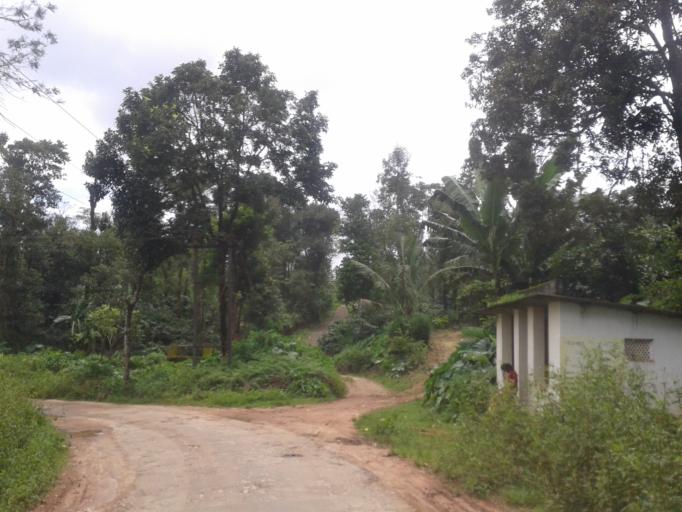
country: IN
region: Karnataka
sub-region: Chikmagalur
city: Mudigere
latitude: 13.0118
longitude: 75.6557
